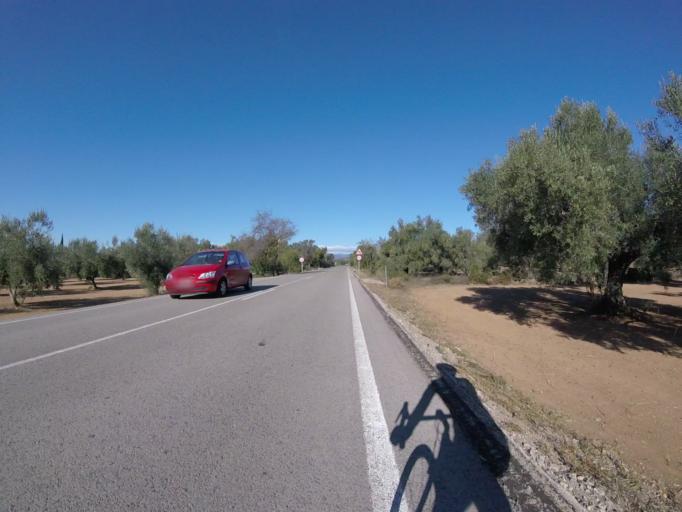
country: ES
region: Valencia
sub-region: Provincia de Castello
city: Cervera del Maestre
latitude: 40.4762
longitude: 0.2233
